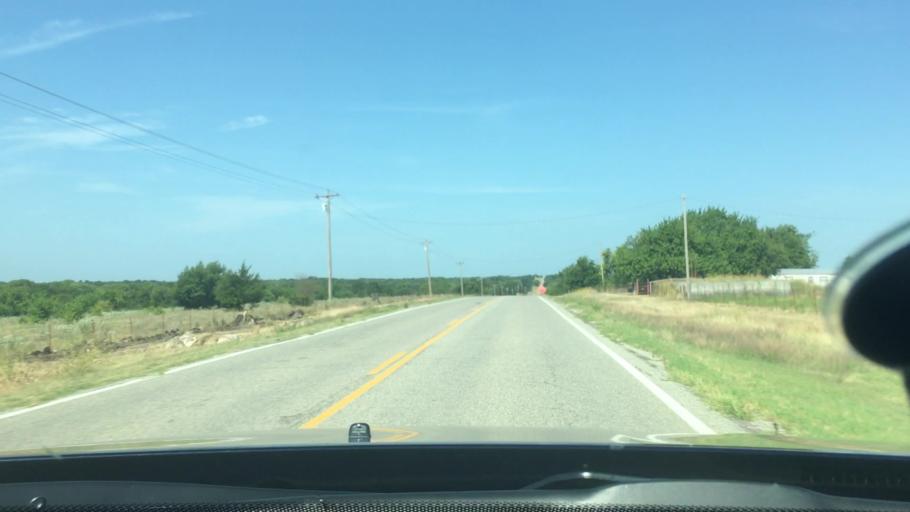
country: US
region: Oklahoma
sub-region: Marshall County
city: Kingston
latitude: 33.9984
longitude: -96.8154
